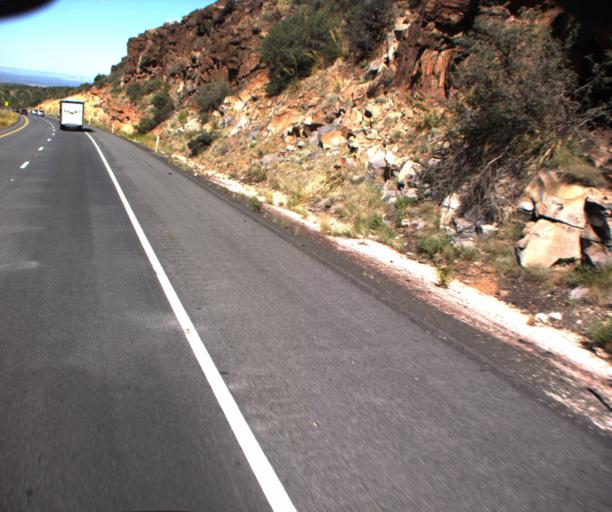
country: US
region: Arizona
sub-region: Coconino County
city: Williams
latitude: 35.2225
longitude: -112.3303
